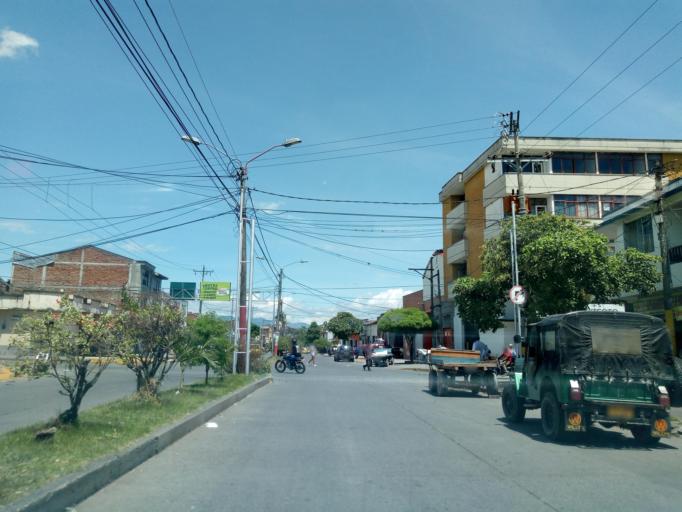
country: CO
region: Valle del Cauca
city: Cartago
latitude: 4.7472
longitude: -75.9157
